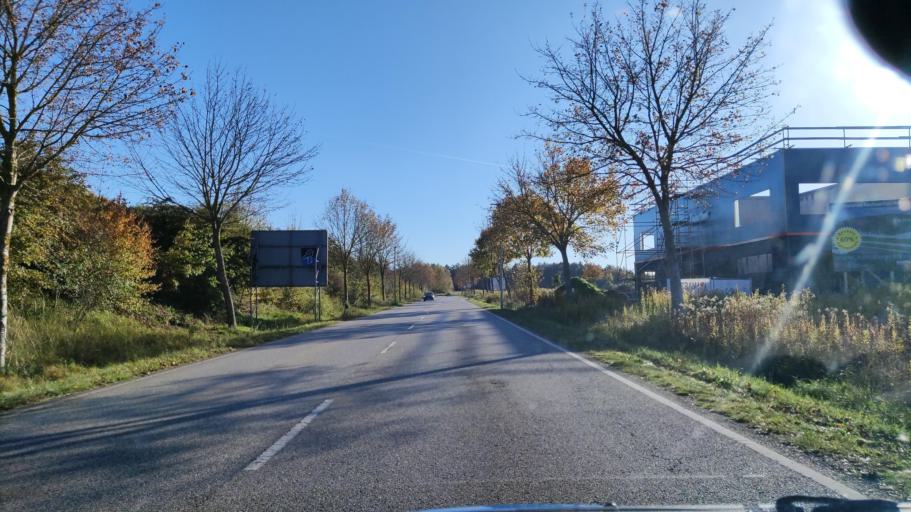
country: DE
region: Schleswig-Holstein
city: Geesthacht
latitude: 53.4544
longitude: 10.3676
